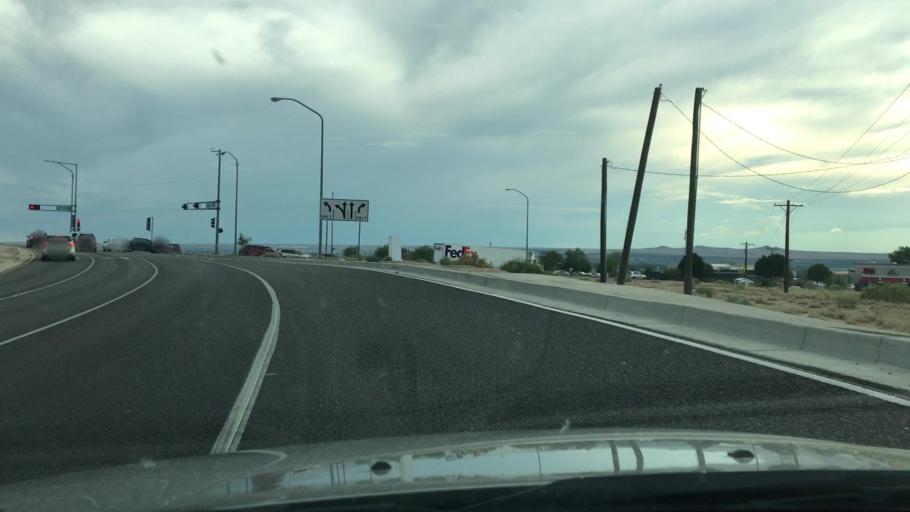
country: US
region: New Mexico
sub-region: Bernalillo County
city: Lee Acres
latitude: 35.1344
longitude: -106.6099
